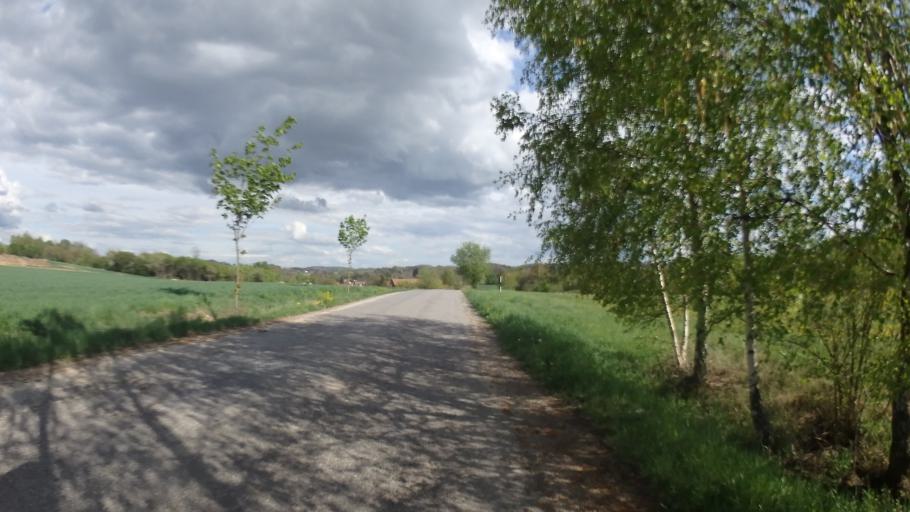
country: CZ
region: Vysocina
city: Merin
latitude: 49.3405
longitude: 15.8937
